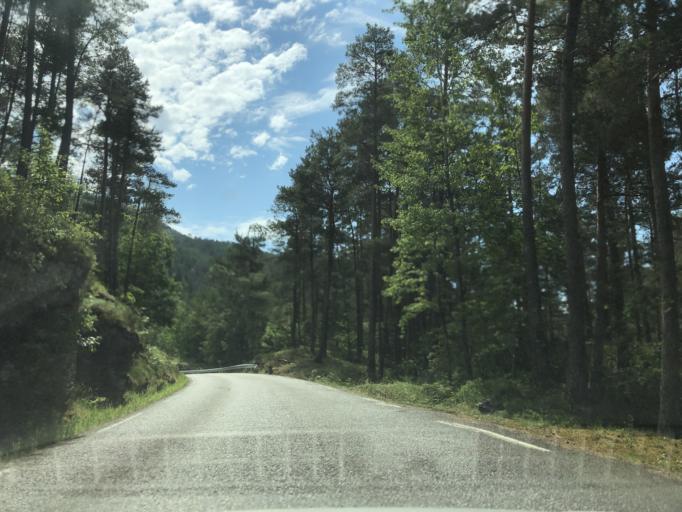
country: NO
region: Hordaland
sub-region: Jondal
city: Jondal
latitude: 60.3082
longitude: 6.2963
